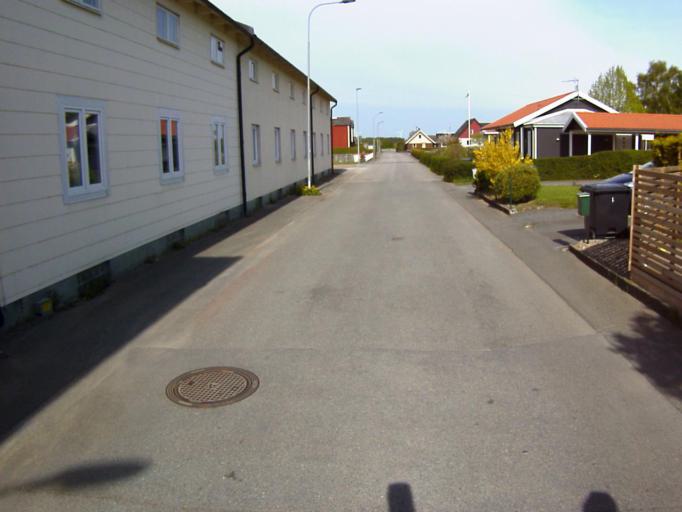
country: SE
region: Skane
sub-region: Kristianstads Kommun
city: Fjalkinge
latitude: 56.0448
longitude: 14.2762
